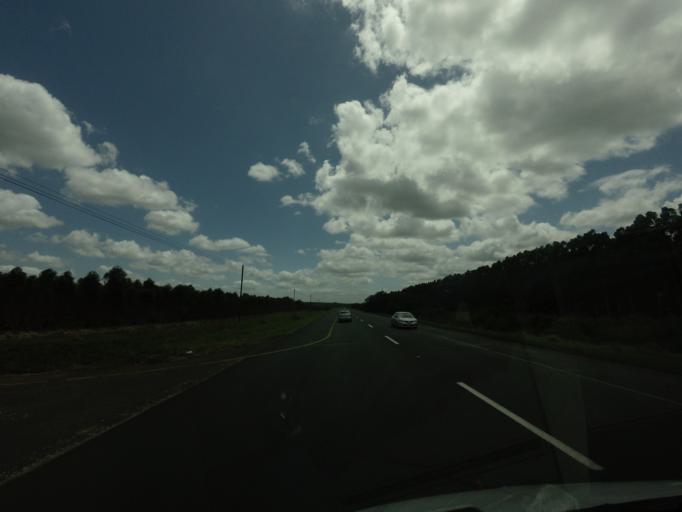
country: ZA
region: KwaZulu-Natal
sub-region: uThungulu District Municipality
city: KwaMbonambi
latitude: -28.5579
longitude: 32.1168
